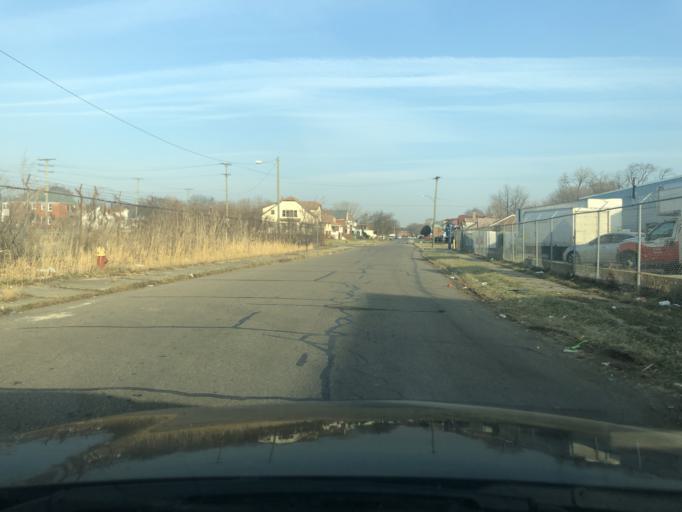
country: US
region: Michigan
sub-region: Wayne County
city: Highland Park
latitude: 42.3982
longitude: -83.1320
